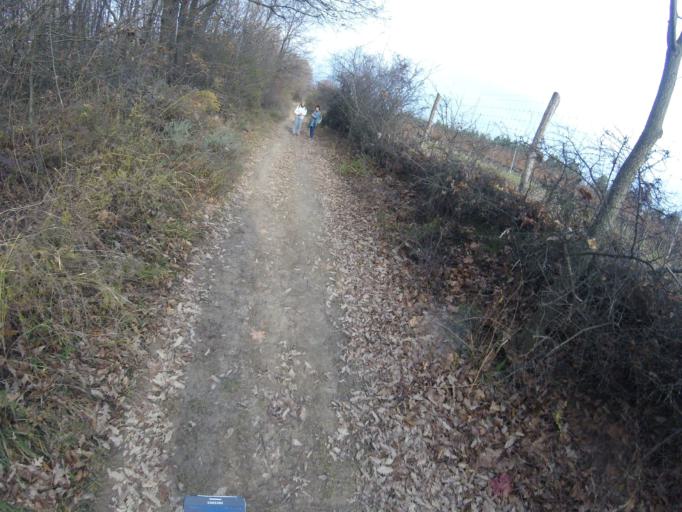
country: HU
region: Tolna
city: Szentgalpuszta
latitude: 46.3457
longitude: 18.6468
